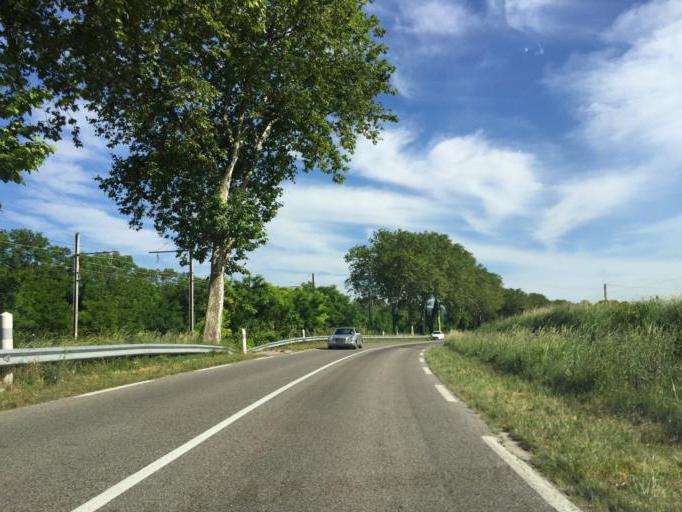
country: FR
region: Rhone-Alpes
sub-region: Departement de la Drome
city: Saulce-sur-Rhone
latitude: 44.6935
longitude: 4.7715
